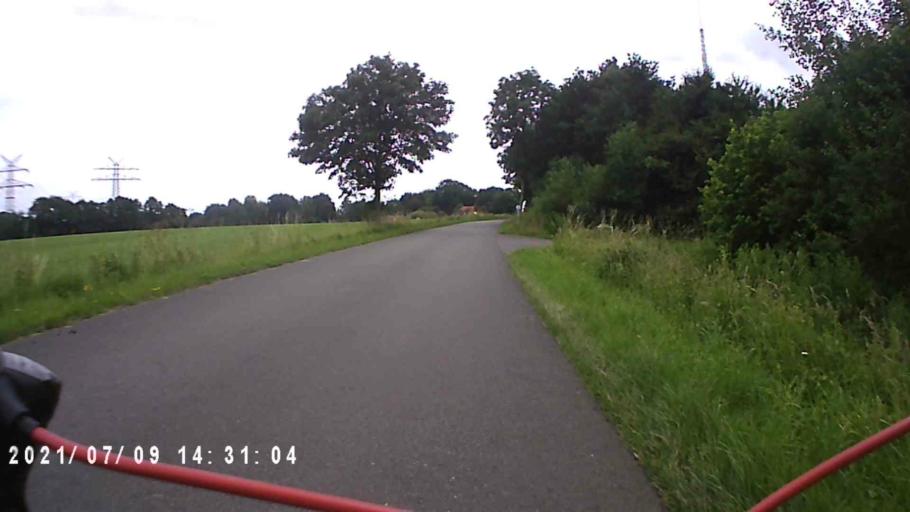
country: DE
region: Lower Saxony
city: Weener
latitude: 53.1271
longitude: 7.3134
